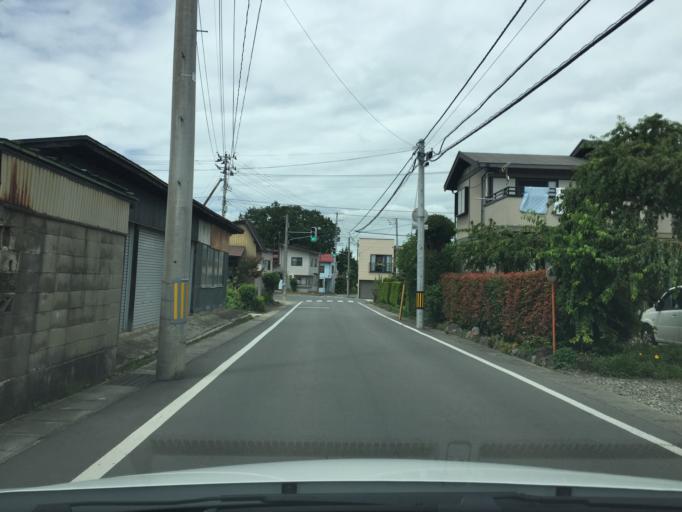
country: JP
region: Yamagata
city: Yonezawa
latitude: 37.8881
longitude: 140.1307
